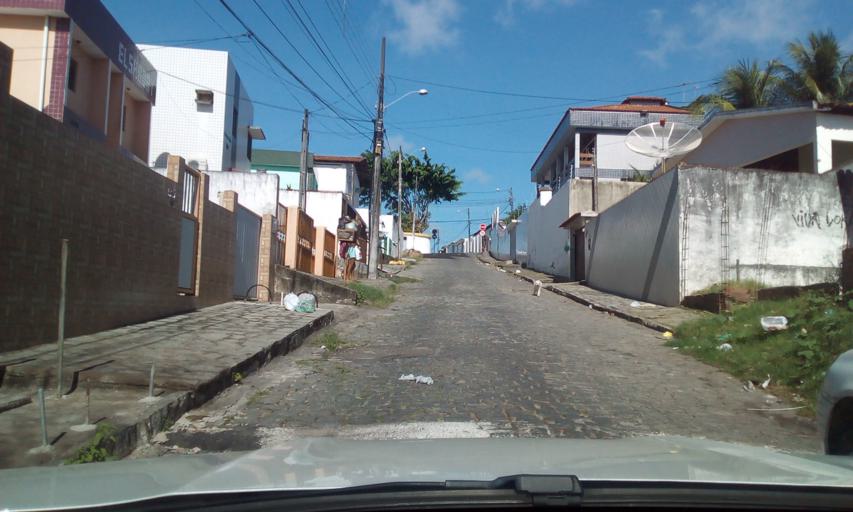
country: BR
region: Paraiba
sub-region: Joao Pessoa
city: Joao Pessoa
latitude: -7.1036
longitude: -34.8596
